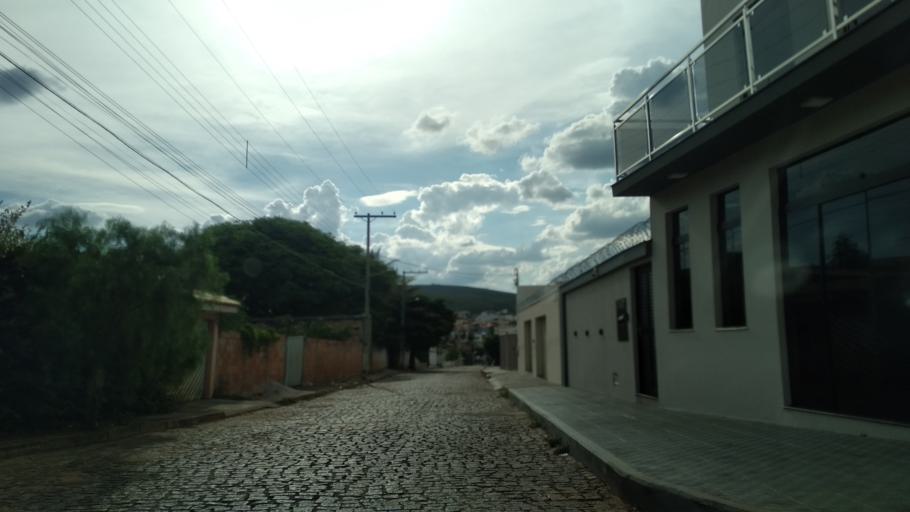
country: BR
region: Bahia
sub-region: Caetite
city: Caetite
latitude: -14.0710
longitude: -42.4804
